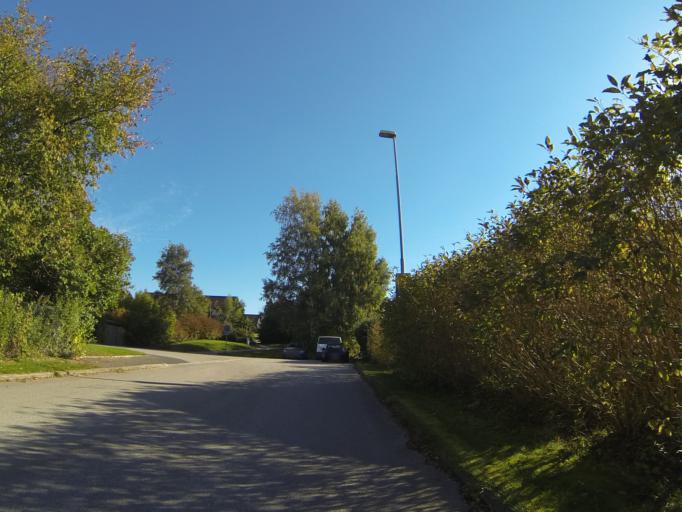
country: SE
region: Skane
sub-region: Lunds Kommun
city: Genarp
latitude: 55.7085
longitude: 13.3305
